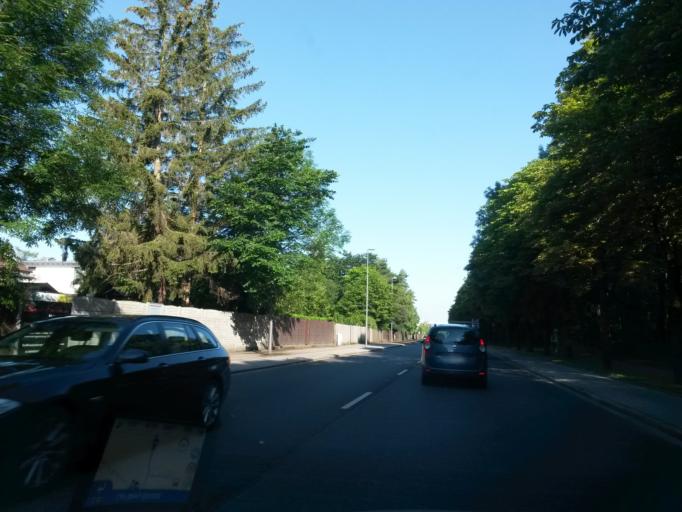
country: DE
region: Bavaria
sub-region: Upper Bavaria
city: Neubiberg
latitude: 48.0894
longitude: 11.6656
